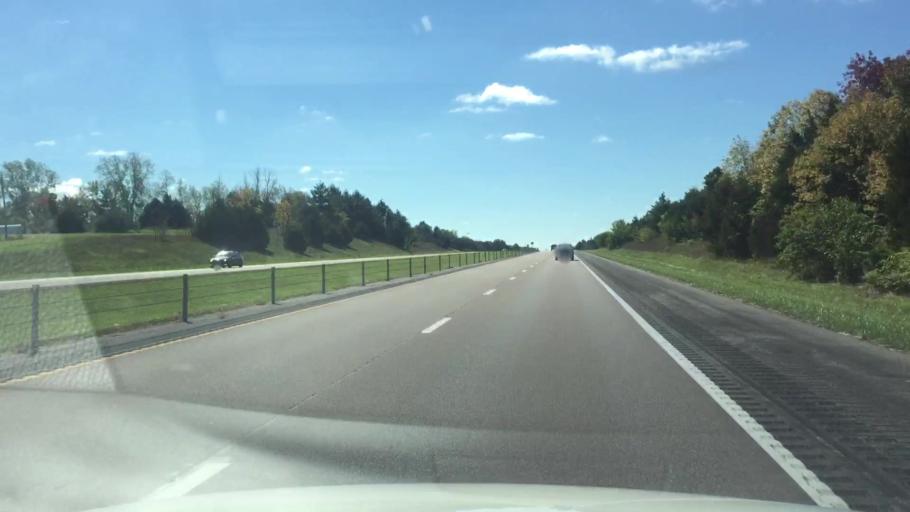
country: US
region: Missouri
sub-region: Boone County
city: Ashland
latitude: 38.7451
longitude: -92.2536
